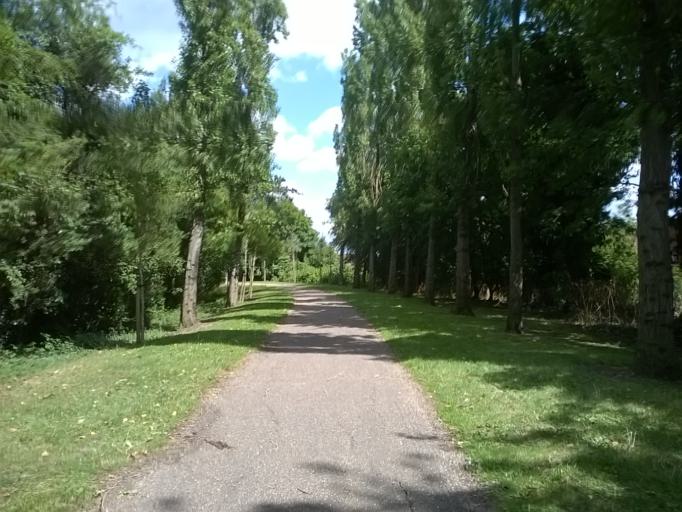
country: GB
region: England
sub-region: Milton Keynes
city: Milton Keynes
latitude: 52.0668
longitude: -0.7451
